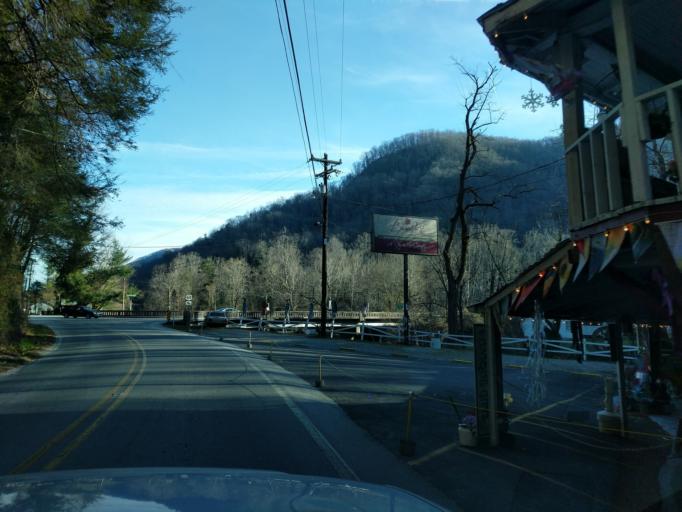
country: US
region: North Carolina
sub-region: Henderson County
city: Edneyville
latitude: 35.4518
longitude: -82.2877
